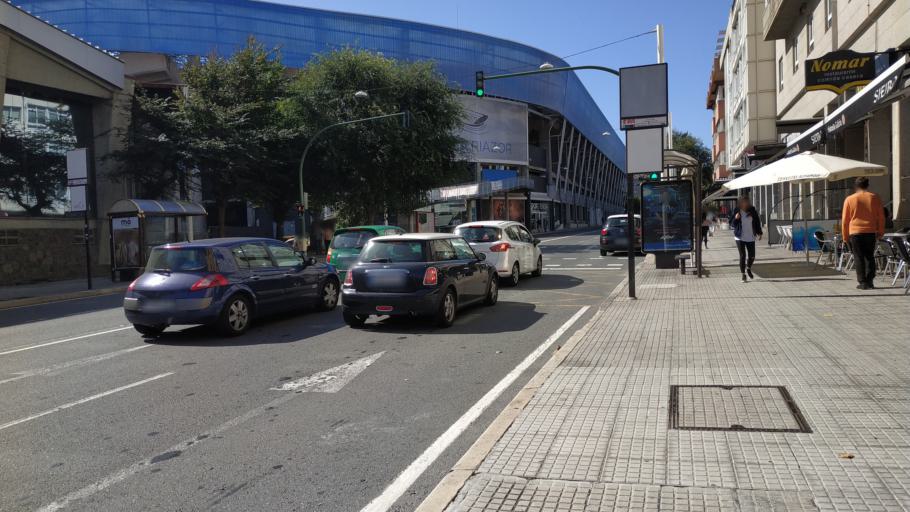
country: ES
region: Galicia
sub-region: Provincia da Coruna
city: A Coruna
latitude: 43.3697
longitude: -8.4160
